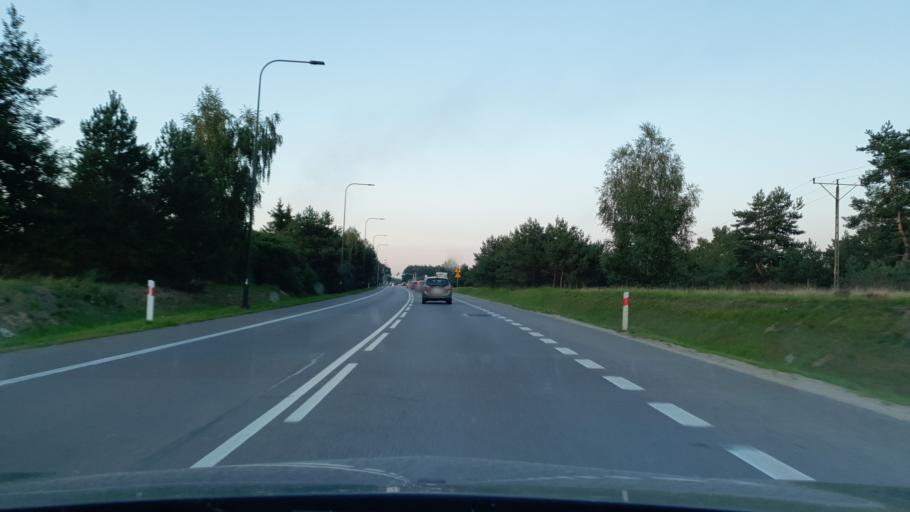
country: PL
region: Pomeranian Voivodeship
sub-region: Powiat leborski
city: Lebork
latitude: 54.5428
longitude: 17.7855
